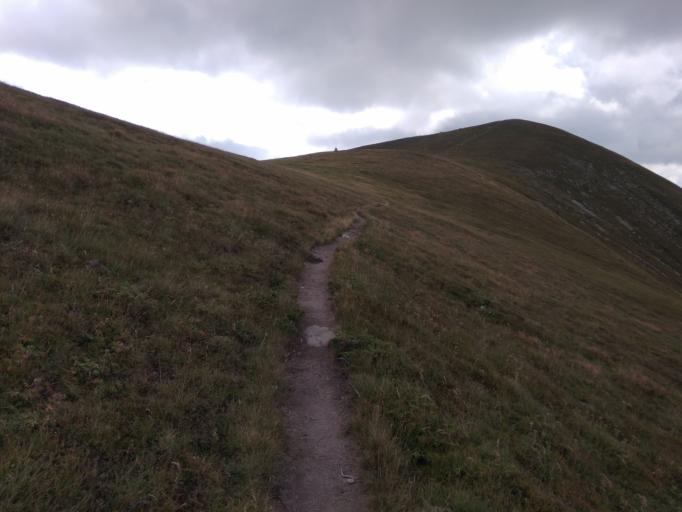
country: BG
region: Plovdiv
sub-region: Obshtina Karlovo
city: Karlovo
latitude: 42.7227
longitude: 24.7857
